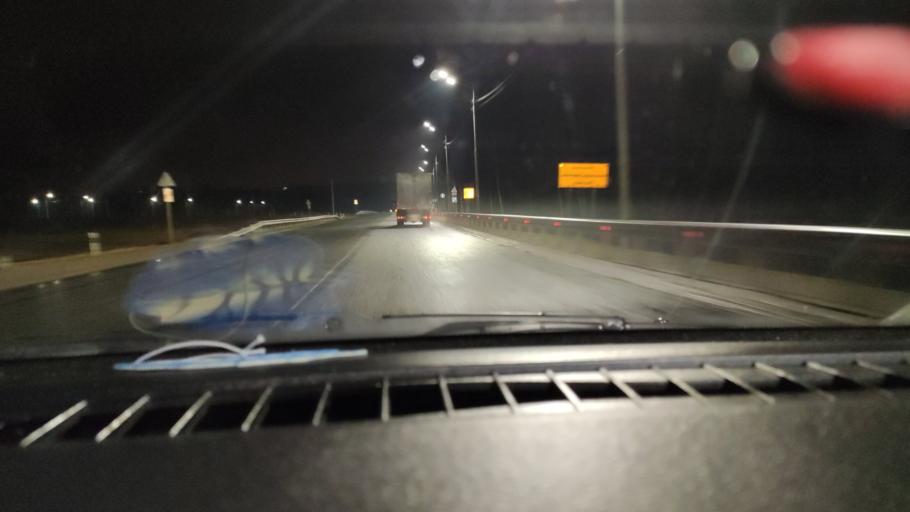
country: RU
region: Udmurtiya
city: Khokhryaki
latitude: 56.9170
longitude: 53.4547
